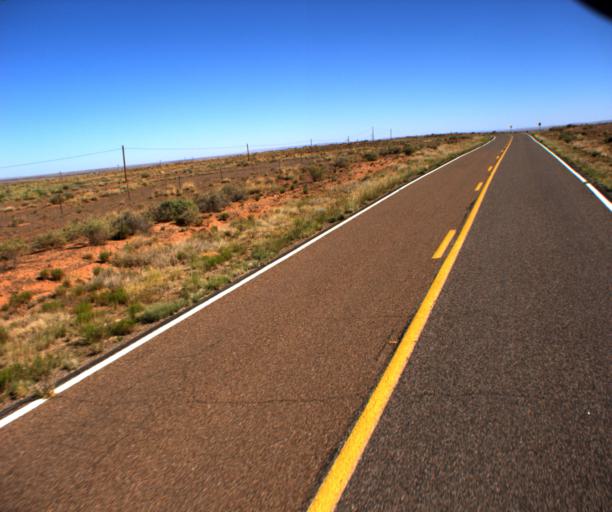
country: US
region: Arizona
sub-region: Coconino County
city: LeChee
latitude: 35.0940
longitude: -110.8607
